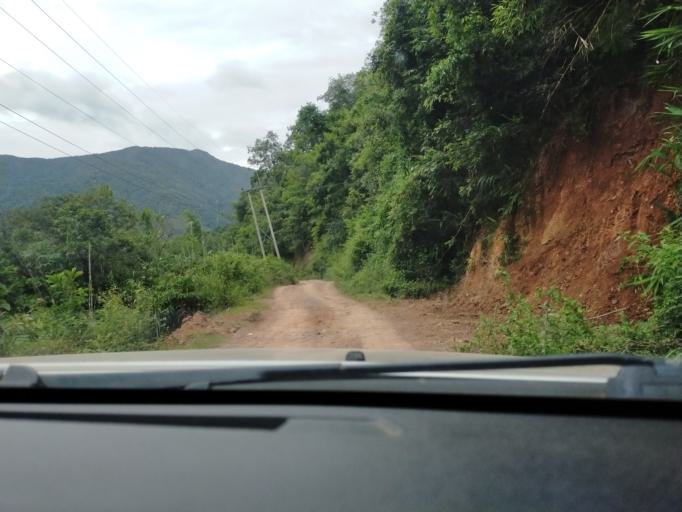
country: TH
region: Nan
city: Chaloem Phra Kiat
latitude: 19.8058
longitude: 101.3617
